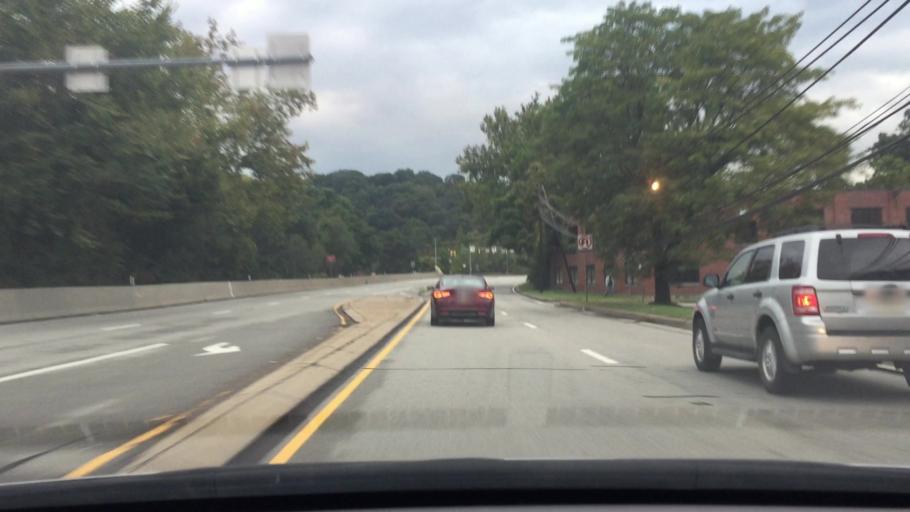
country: US
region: Pennsylvania
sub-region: Allegheny County
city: Jefferson Hills
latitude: 40.2931
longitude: -79.9164
